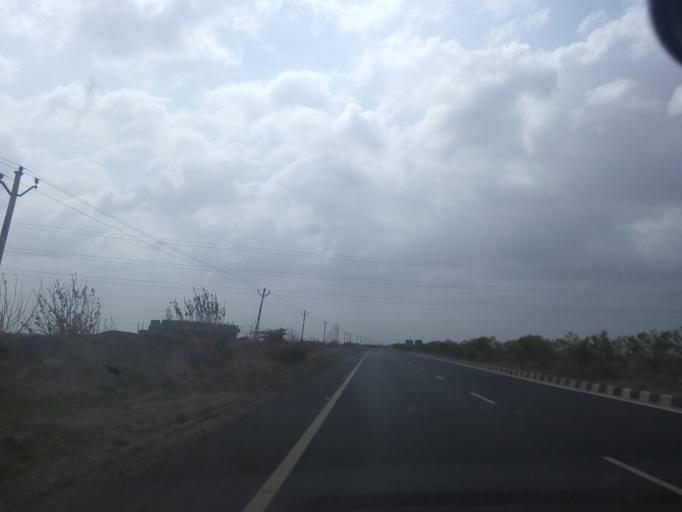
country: IN
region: Gujarat
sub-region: Rajkot
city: Morbi
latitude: 23.0714
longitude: 70.8136
